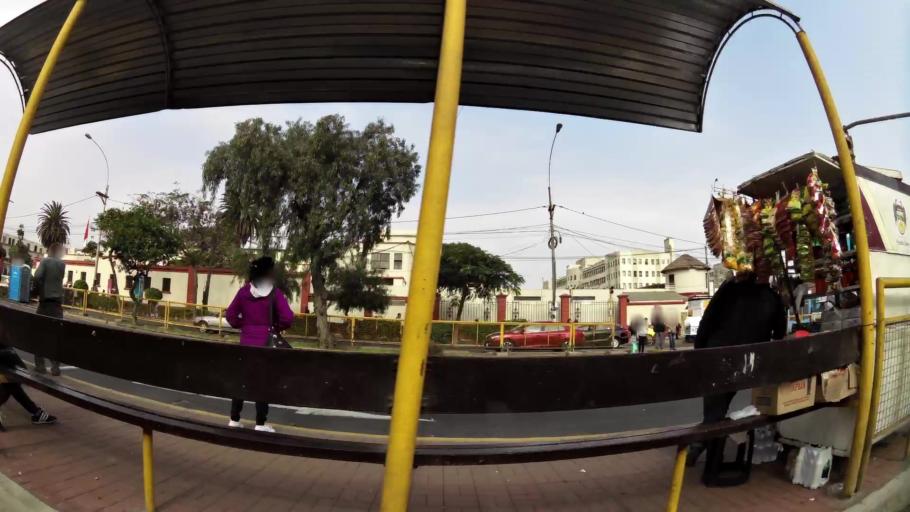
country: PE
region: Lima
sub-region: Lima
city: San Isidro
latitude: -12.0843
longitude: -77.0615
